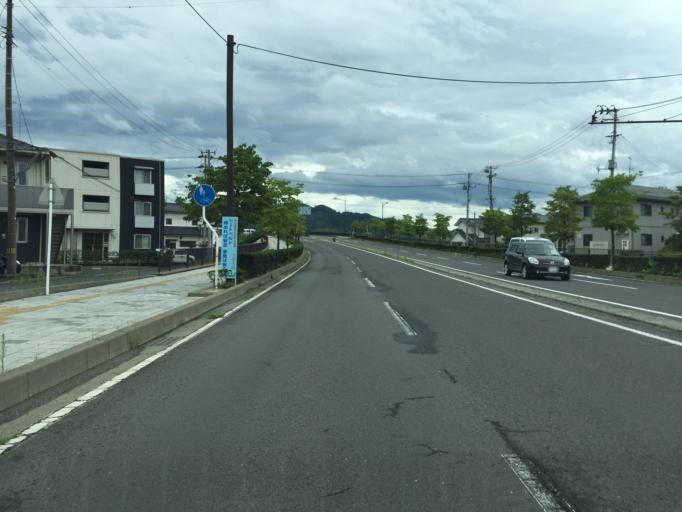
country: JP
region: Fukushima
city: Fukushima-shi
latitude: 37.7550
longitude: 140.4806
